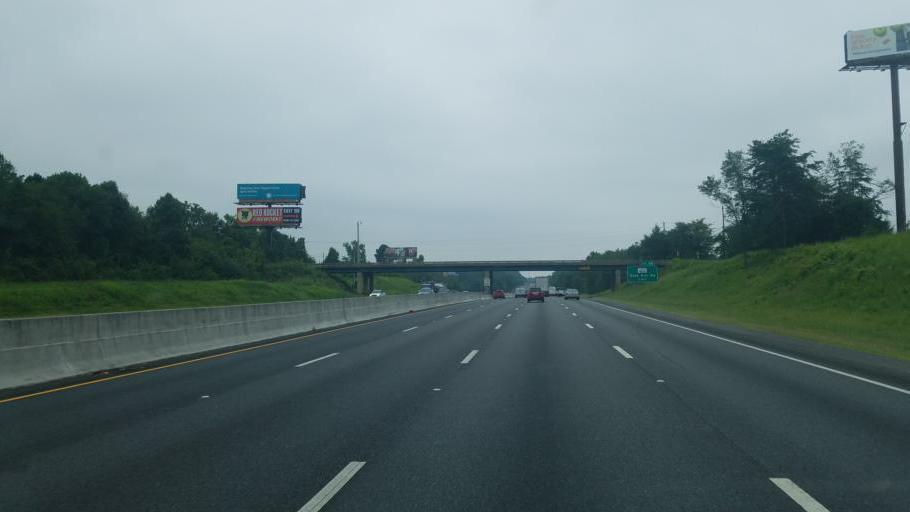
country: US
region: South Carolina
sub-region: York County
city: Fort Mill
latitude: 35.0416
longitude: -80.9598
